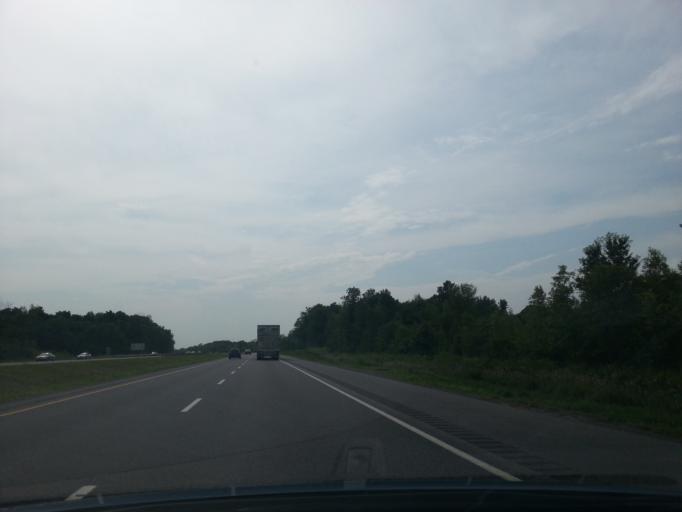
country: CA
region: Quebec
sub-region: Monteregie
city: Mercier
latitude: 45.3371
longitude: -73.7886
